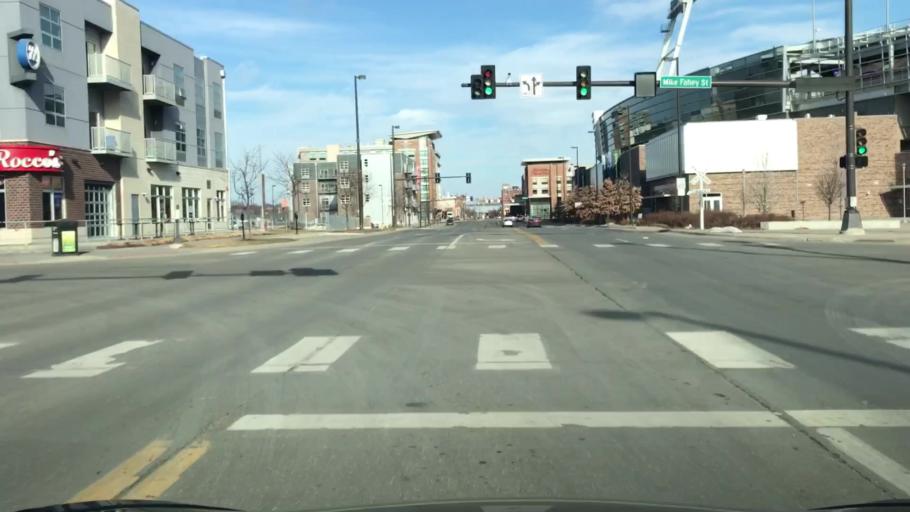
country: US
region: Nebraska
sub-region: Douglas County
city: Omaha
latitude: 41.2657
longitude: -95.9331
